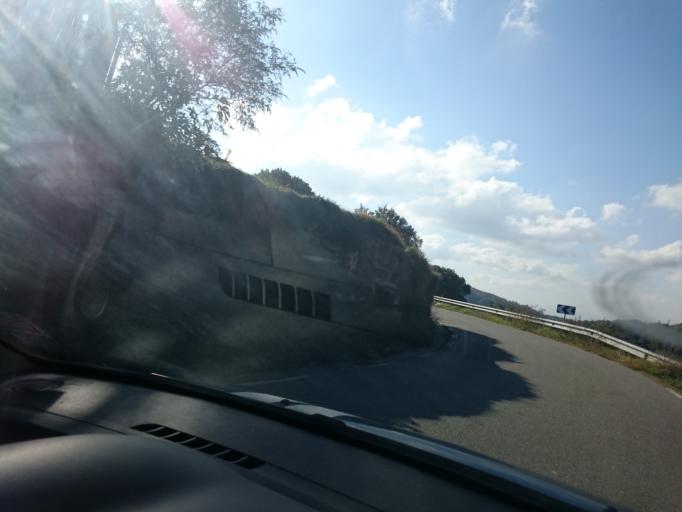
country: ES
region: Catalonia
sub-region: Provincia de Barcelona
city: Santa Maria de Corco
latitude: 42.0342
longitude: 2.3755
